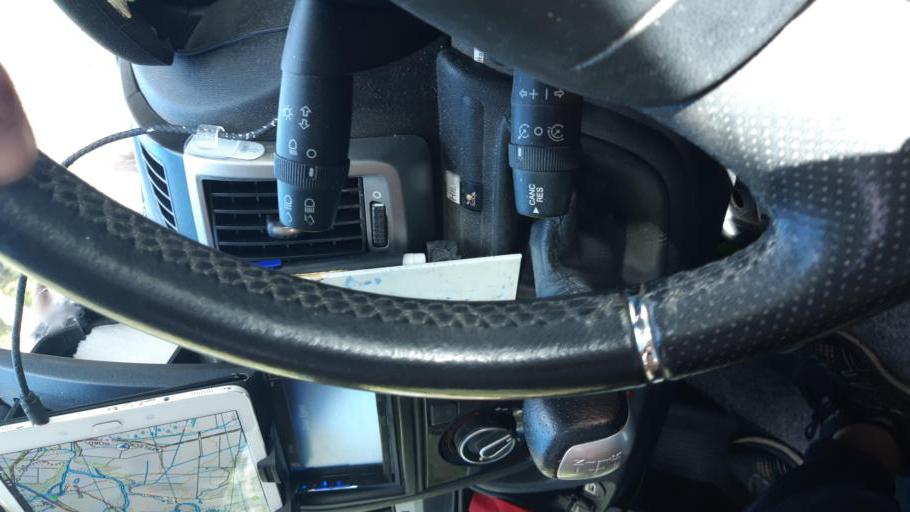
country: NZ
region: Southland
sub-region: Southland District
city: Winton
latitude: -45.7837
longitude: 168.1755
